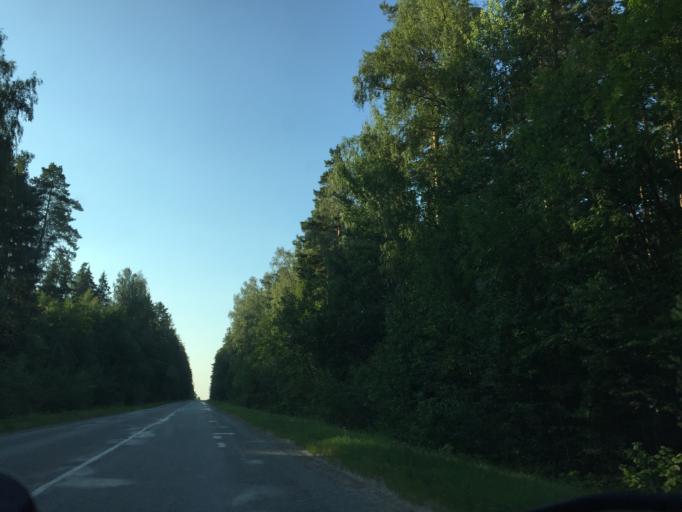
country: LV
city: Tervete
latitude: 56.4601
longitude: 23.4057
